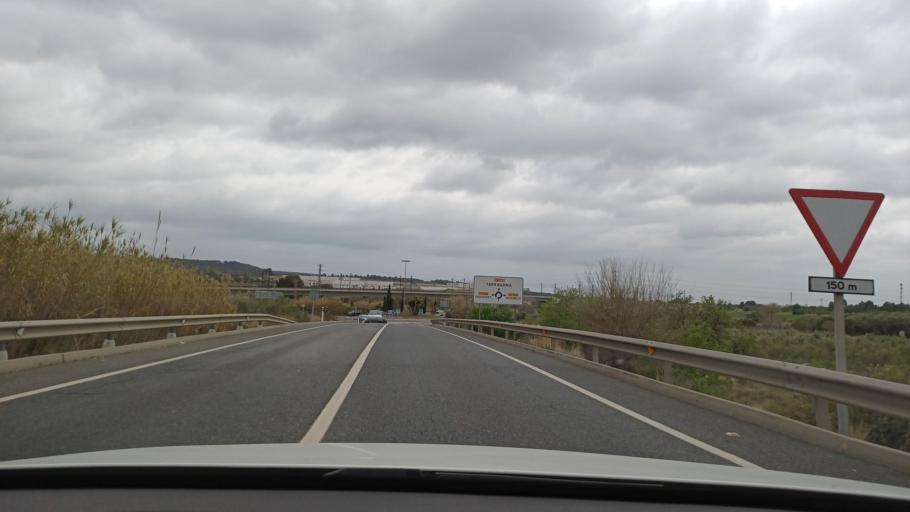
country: ES
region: Catalonia
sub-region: Provincia de Tarragona
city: la Pobla de Mafumet
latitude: 41.1948
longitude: 1.2430
